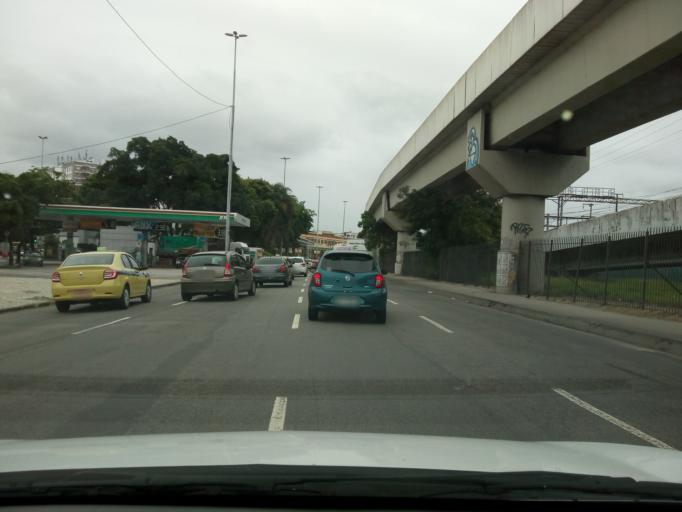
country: BR
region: Rio de Janeiro
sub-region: Rio De Janeiro
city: Rio de Janeiro
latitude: -22.9105
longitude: -43.2159
